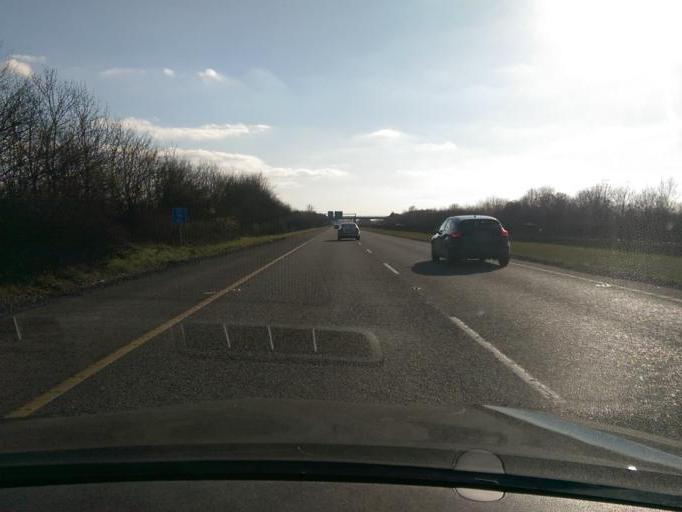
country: IE
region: Leinster
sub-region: Kildare
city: Kilcullen
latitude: 53.1892
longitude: -6.7289
